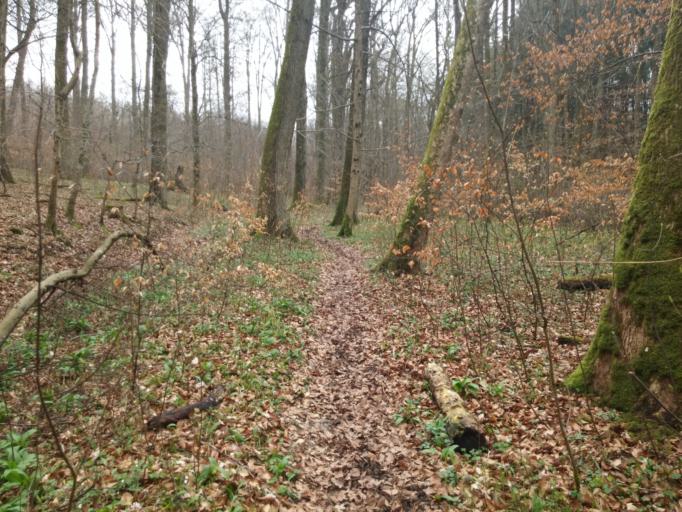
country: DE
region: Baden-Wuerttemberg
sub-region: Regierungsbezirk Stuttgart
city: Wernau
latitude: 48.6969
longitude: 9.4348
